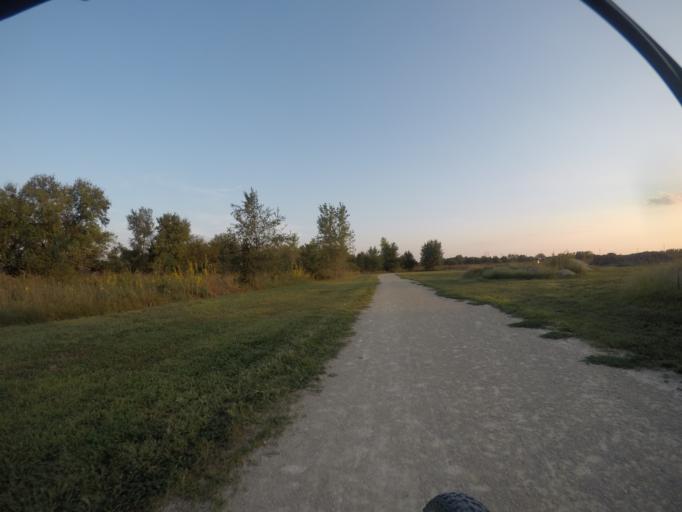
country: US
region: Kansas
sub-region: Riley County
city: Manhattan
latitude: 39.2012
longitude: -96.5448
